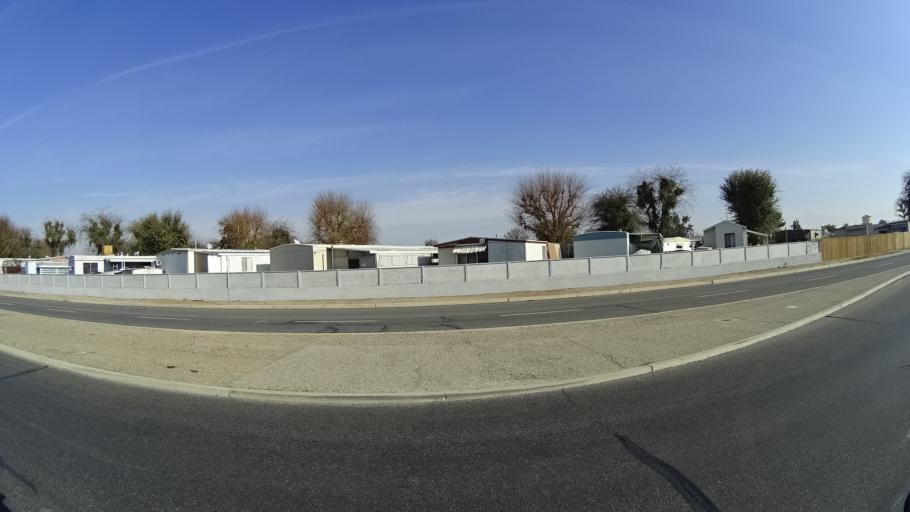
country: US
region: California
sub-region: Kern County
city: Bakersfield
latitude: 35.3234
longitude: -119.0084
